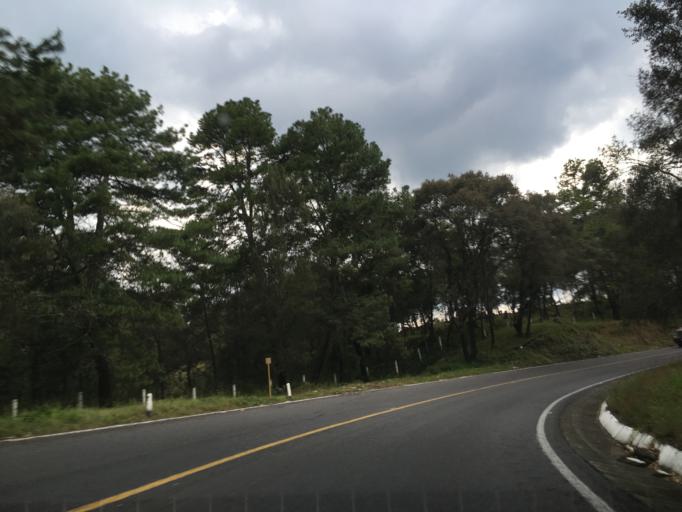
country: MX
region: Michoacan
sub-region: Patzcuaro
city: Santa Maria Huiramangaro (San Juan Tumbio)
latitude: 19.4966
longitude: -101.7106
